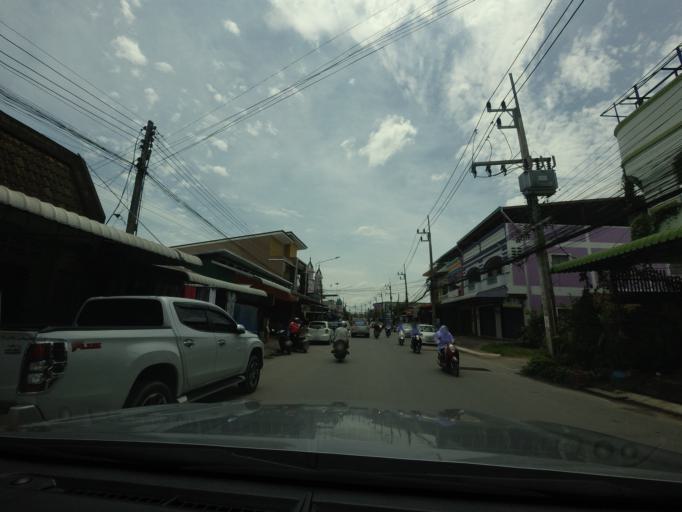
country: TH
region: Yala
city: Yala
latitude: 6.5389
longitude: 101.2931
